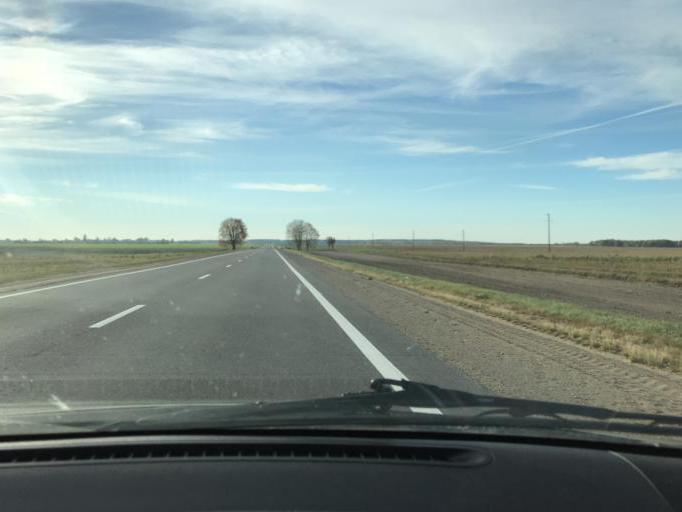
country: BY
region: Brest
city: Ivanava
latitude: 52.1560
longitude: 25.6698
